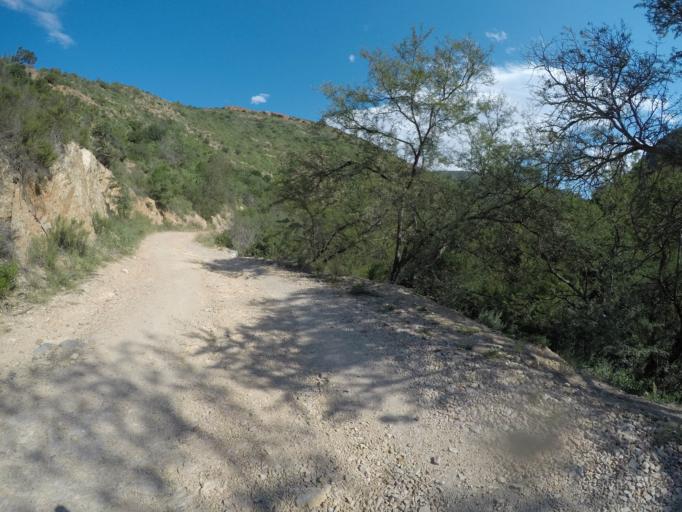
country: ZA
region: Eastern Cape
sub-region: Cacadu District Municipality
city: Kareedouw
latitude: -33.6548
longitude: 24.3634
